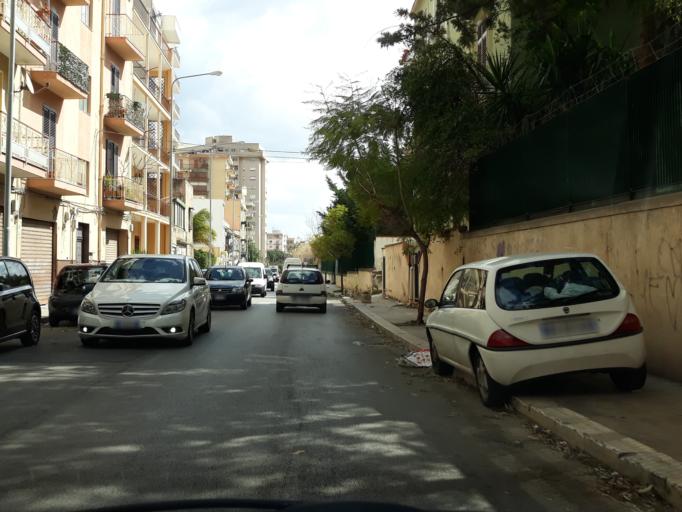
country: IT
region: Sicily
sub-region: Palermo
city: Palermo
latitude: 38.1228
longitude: 13.3250
